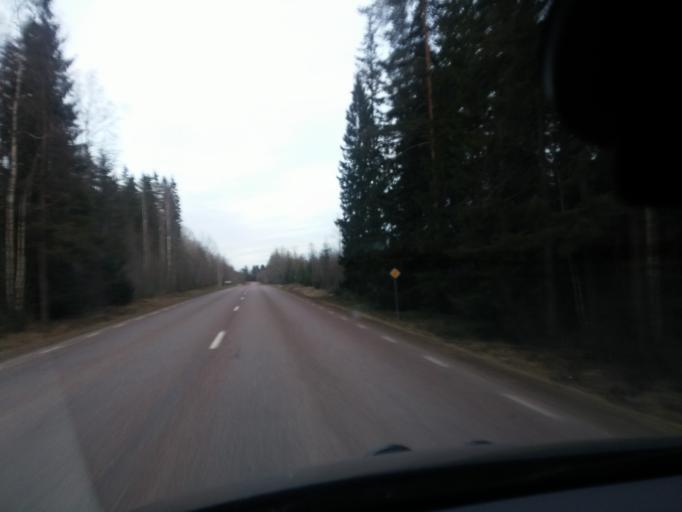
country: SE
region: Dalarna
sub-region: Faluns Kommun
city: Bjursas
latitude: 60.7277
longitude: 15.4291
